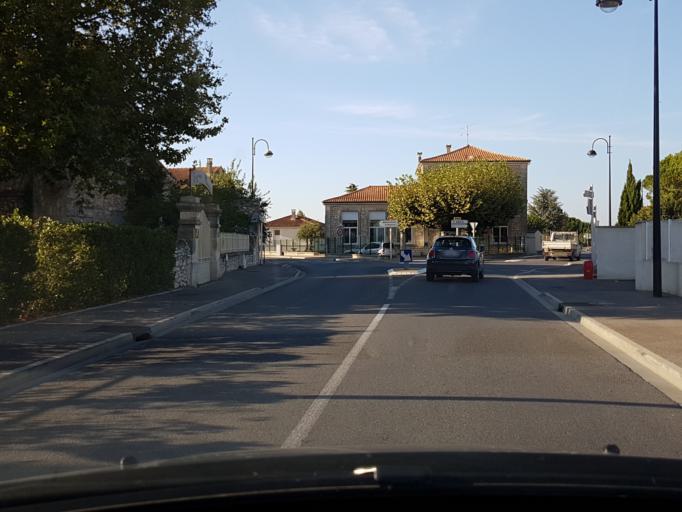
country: FR
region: Provence-Alpes-Cote d'Azur
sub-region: Departement des Bouches-du-Rhone
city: Molleges
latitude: 43.8071
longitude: 4.9491
